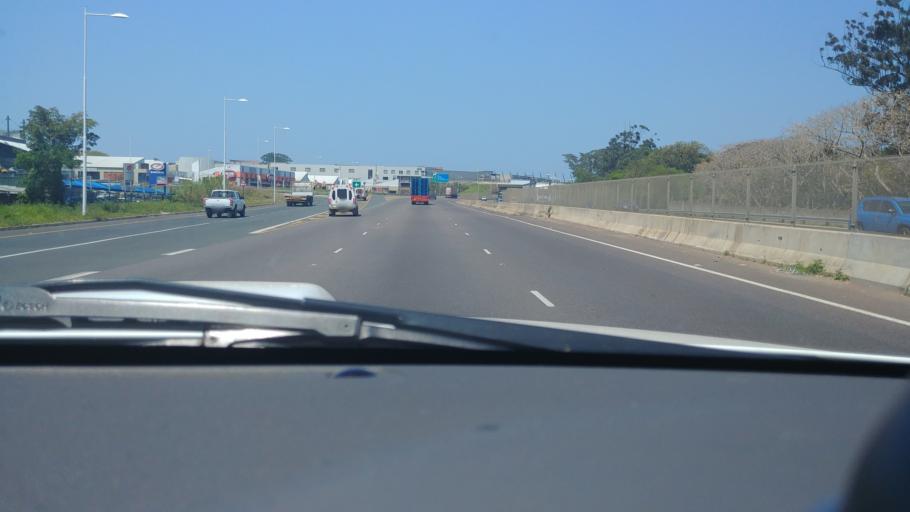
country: ZA
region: KwaZulu-Natal
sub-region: eThekwini Metropolitan Municipality
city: Durban
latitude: -29.7090
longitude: 31.0475
